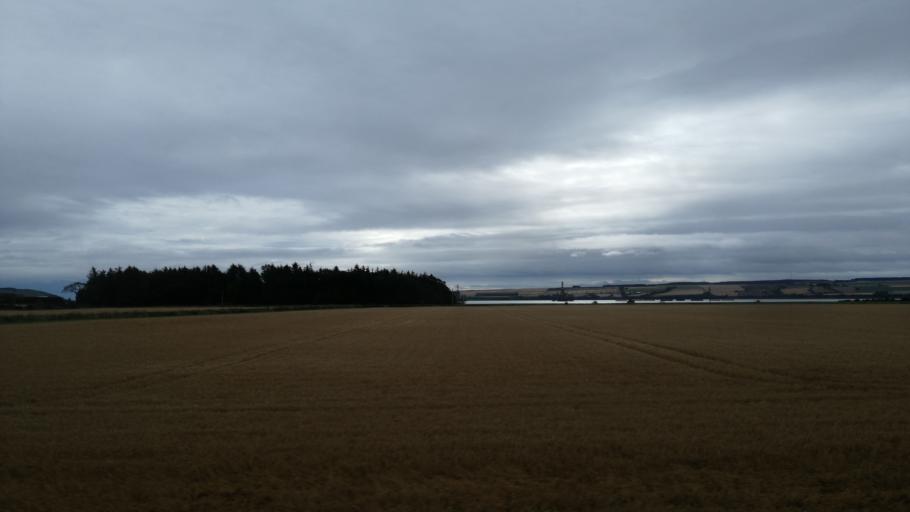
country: GB
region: Scotland
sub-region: Highland
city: Invergordon
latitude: 57.7105
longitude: -4.1336
